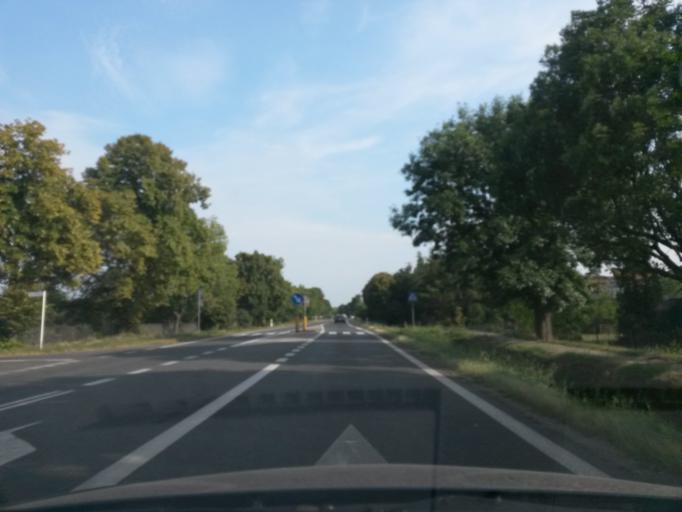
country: PL
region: Masovian Voivodeship
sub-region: Powiat sierpecki
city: Sierpc
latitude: 52.8577
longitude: 19.6816
